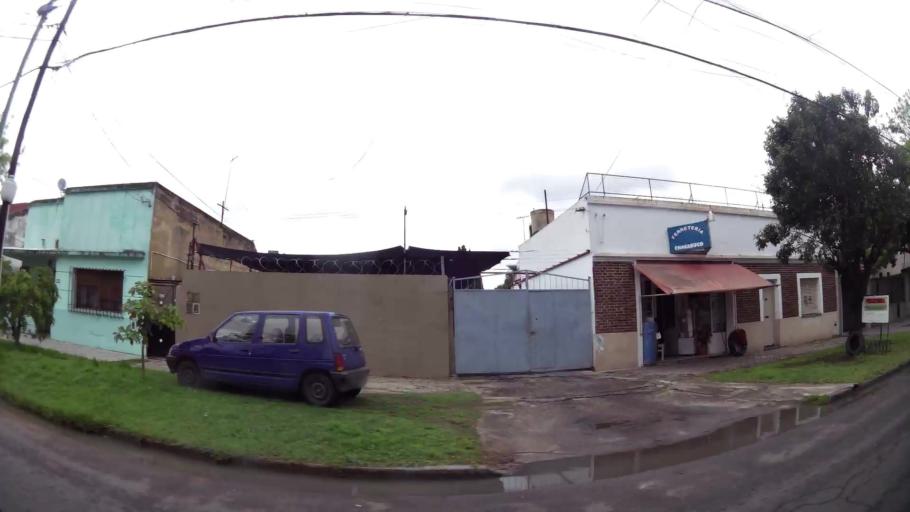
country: AR
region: Buenos Aires
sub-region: Partido de Lomas de Zamora
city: Lomas de Zamora
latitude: -34.7469
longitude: -58.3844
